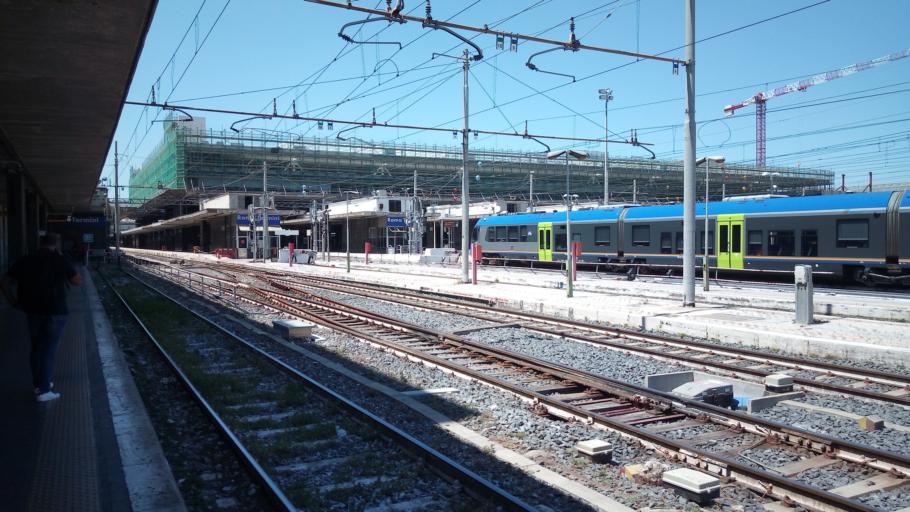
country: IT
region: Latium
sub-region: Citta metropolitana di Roma Capitale
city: Rome
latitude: 41.8977
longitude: 12.5061
